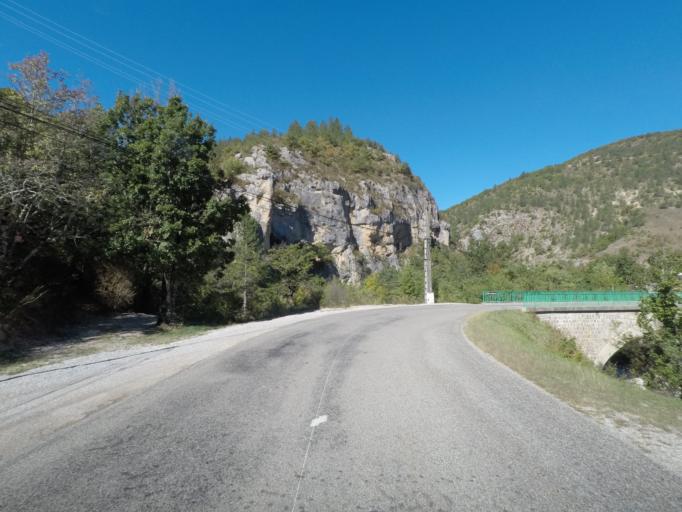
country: FR
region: Rhone-Alpes
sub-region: Departement de la Drome
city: Die
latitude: 44.6286
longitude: 5.3025
